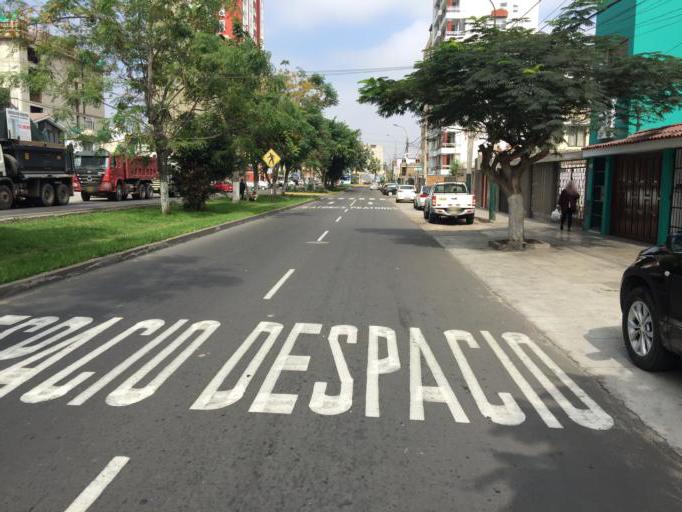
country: PE
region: Lima
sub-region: Lima
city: Surco
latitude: -12.1192
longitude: -77.0047
